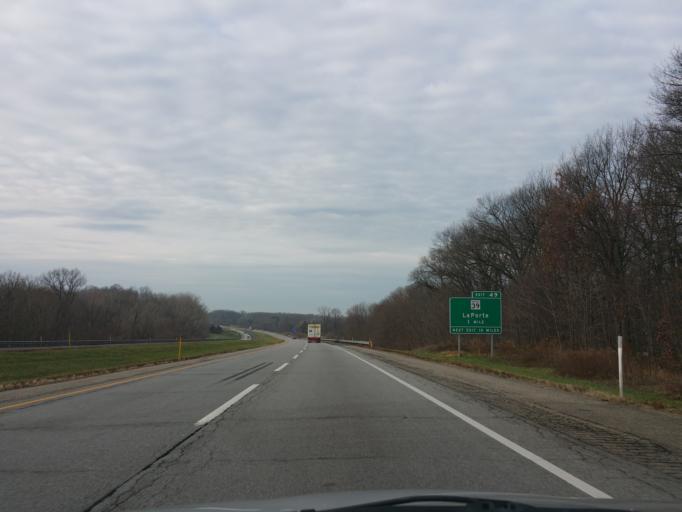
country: US
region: Indiana
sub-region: LaPorte County
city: LaPorte
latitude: 41.6739
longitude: -86.7074
